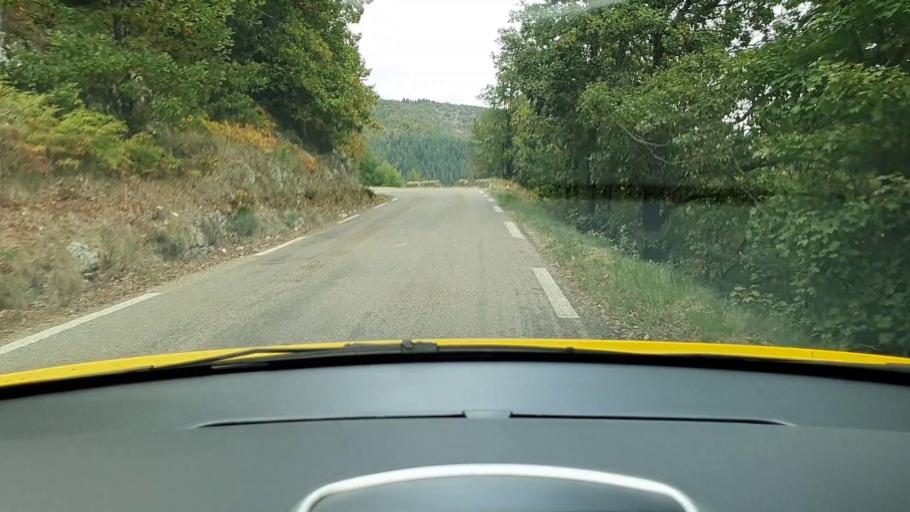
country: FR
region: Languedoc-Roussillon
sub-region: Departement du Gard
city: Le Vigan
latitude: 44.0301
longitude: 3.5744
